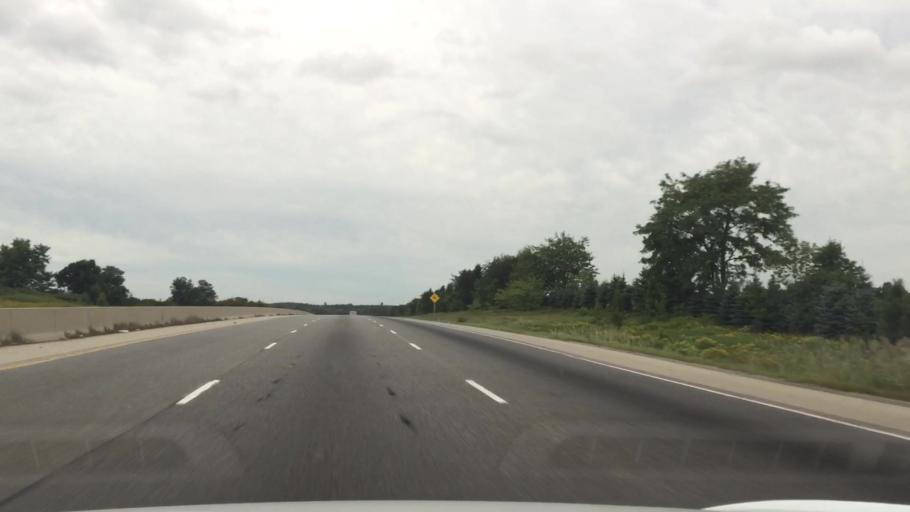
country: CA
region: Ontario
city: Kitchener
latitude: 43.2886
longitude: -80.5074
